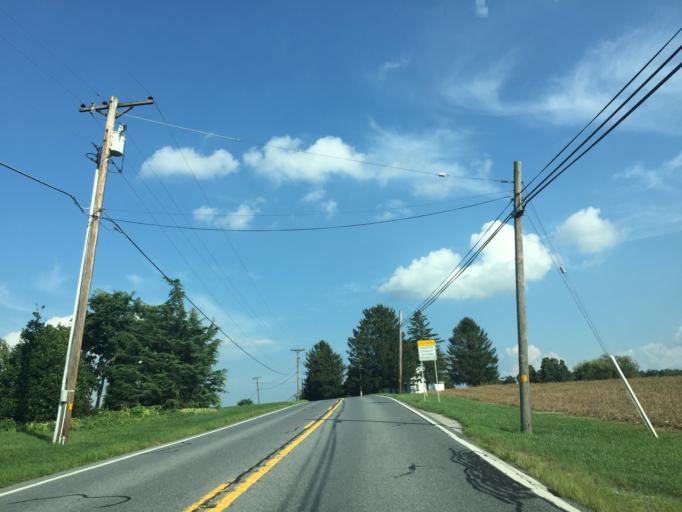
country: US
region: Maryland
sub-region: Carroll County
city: Hampstead
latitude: 39.6003
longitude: -76.7709
